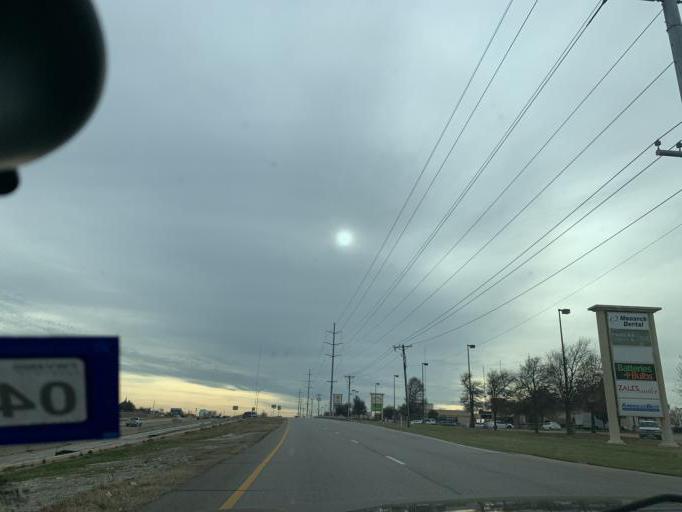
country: US
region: Texas
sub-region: Dallas County
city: Cedar Hill
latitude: 32.6037
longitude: -96.9327
